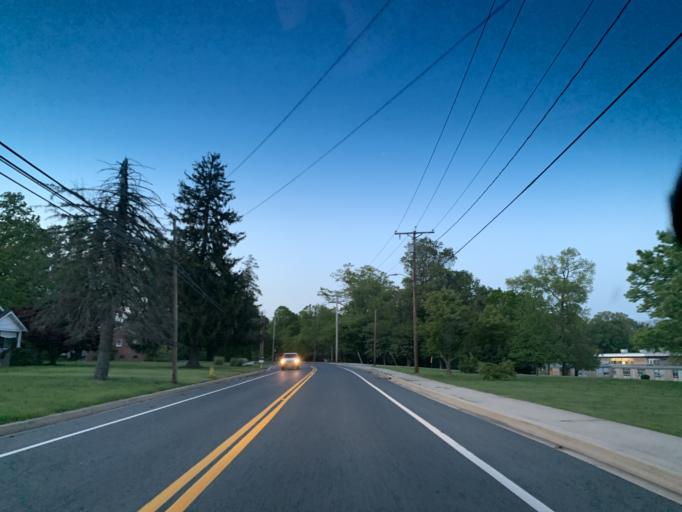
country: US
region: Maryland
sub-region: Harford County
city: Aberdeen
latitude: 39.5172
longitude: -76.1720
